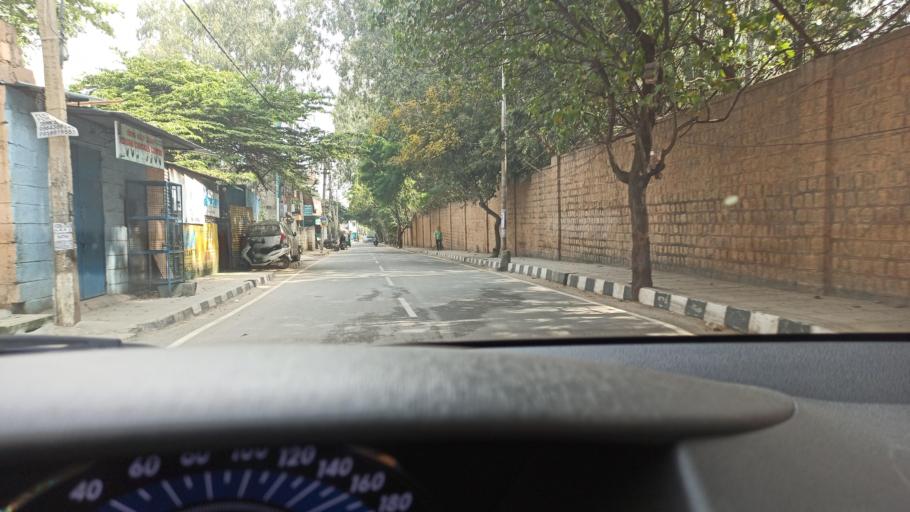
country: IN
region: Karnataka
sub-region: Bangalore Urban
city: Bangalore
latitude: 12.9886
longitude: 77.6808
